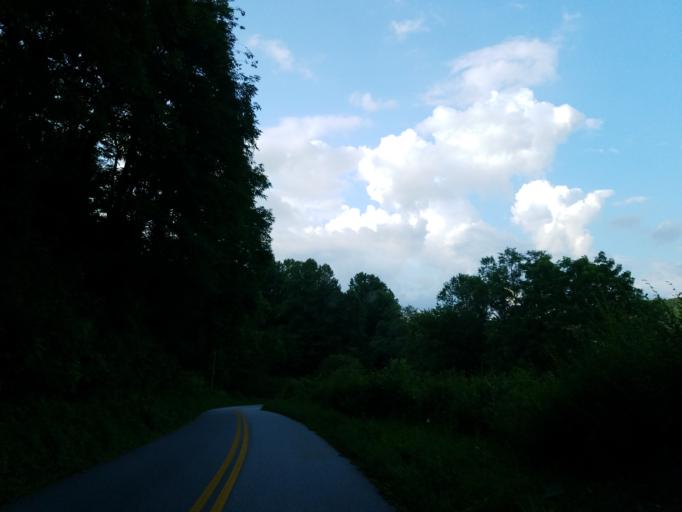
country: US
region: Georgia
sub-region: Lumpkin County
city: Dahlonega
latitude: 34.6905
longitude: -84.0793
